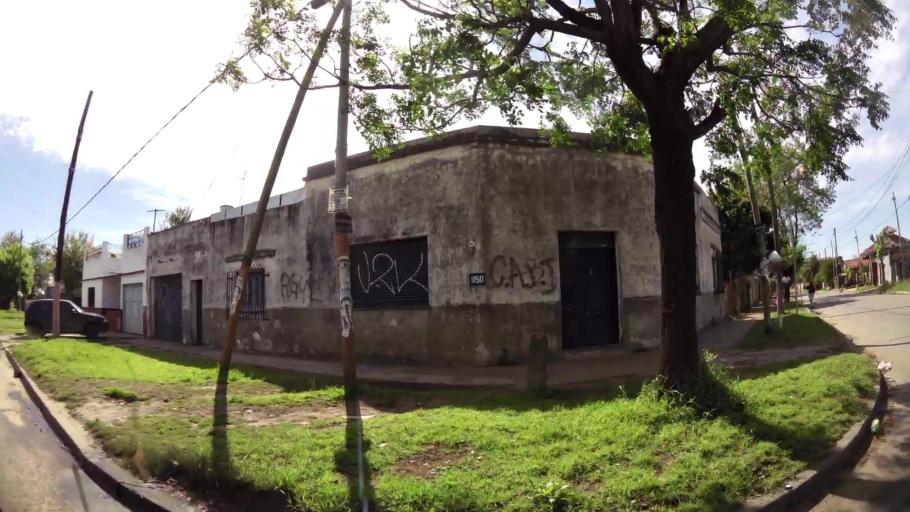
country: AR
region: Buenos Aires
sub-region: Partido de Quilmes
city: Quilmes
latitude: -34.7727
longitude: -58.2894
